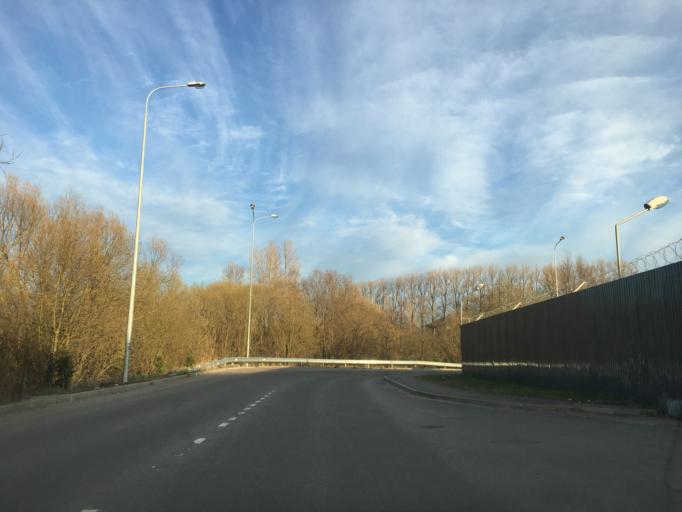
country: RU
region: St.-Petersburg
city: Uritsk
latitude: 59.8439
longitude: 30.1819
